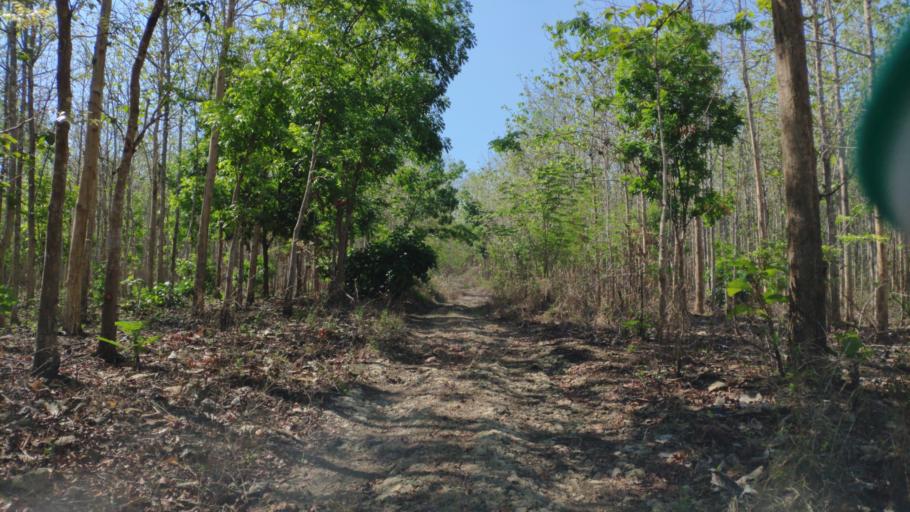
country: ID
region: Central Java
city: Botoh
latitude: -7.0849
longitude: 111.4528
